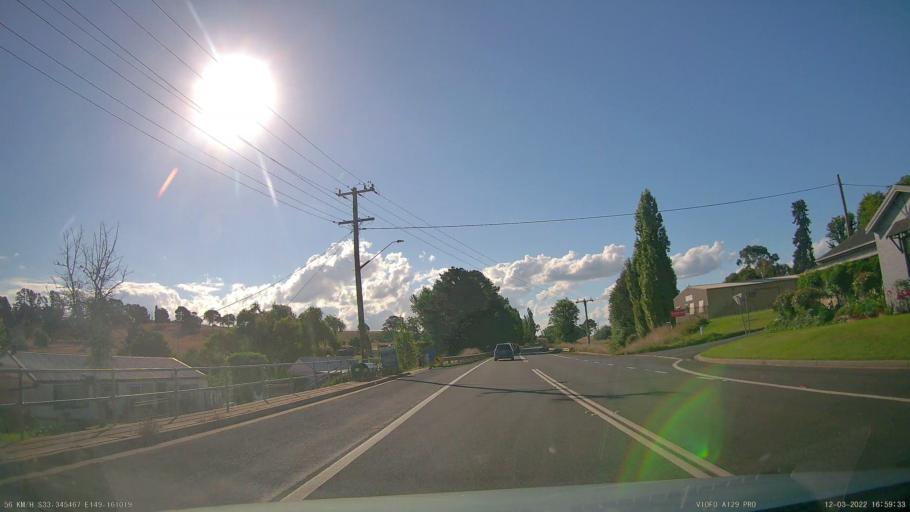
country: AU
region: New South Wales
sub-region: Orange Municipality
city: Orange
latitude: -33.3454
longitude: 149.1609
